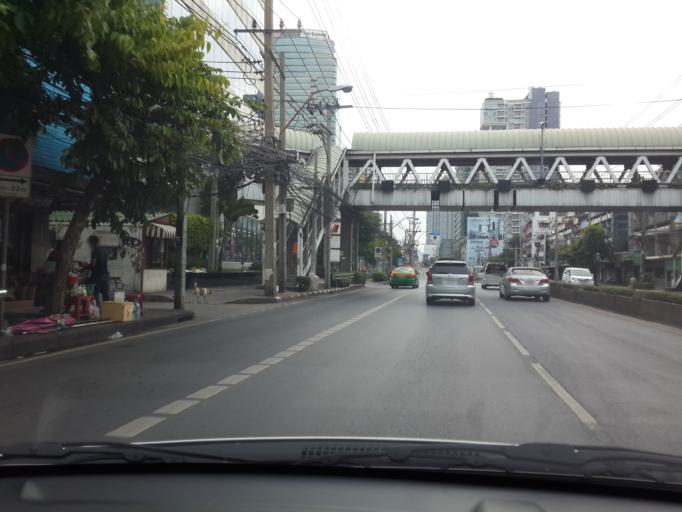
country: TH
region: Bangkok
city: Watthana
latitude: 13.7479
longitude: 100.5707
